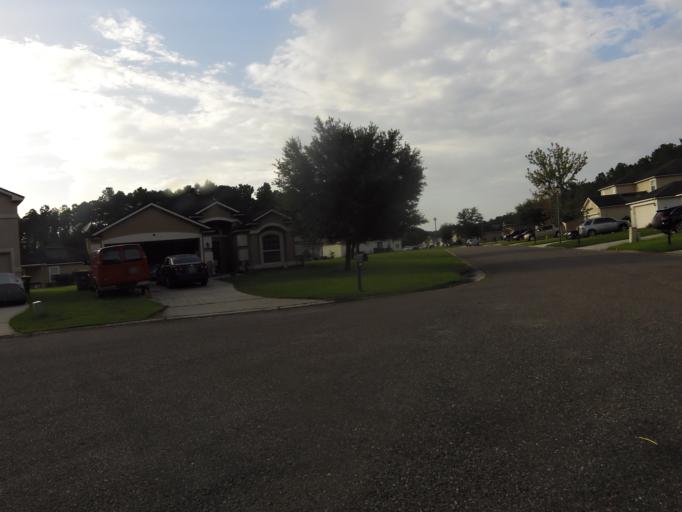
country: US
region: Florida
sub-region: Duval County
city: Jacksonville
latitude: 30.3551
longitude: -81.7696
